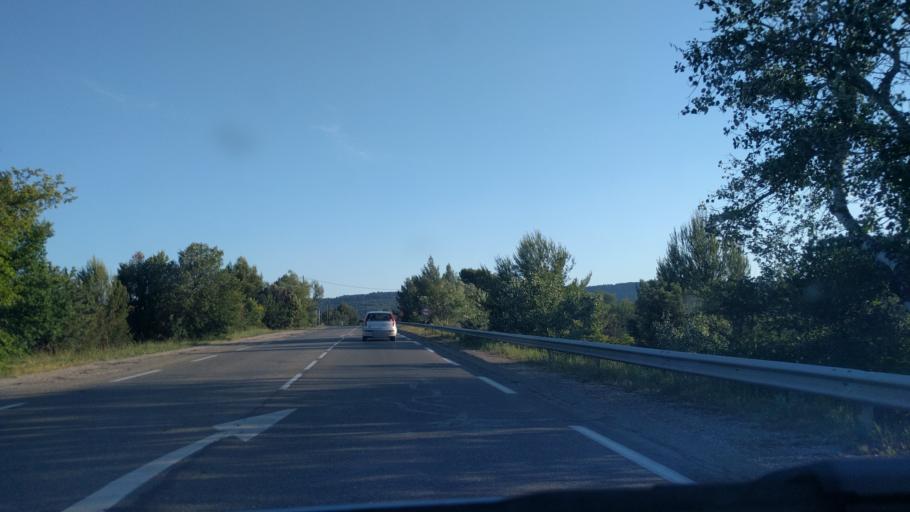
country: FR
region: Provence-Alpes-Cote d'Azur
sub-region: Departement des Bouches-du-Rhone
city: Meyrargues
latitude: 43.6375
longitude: 5.4894
